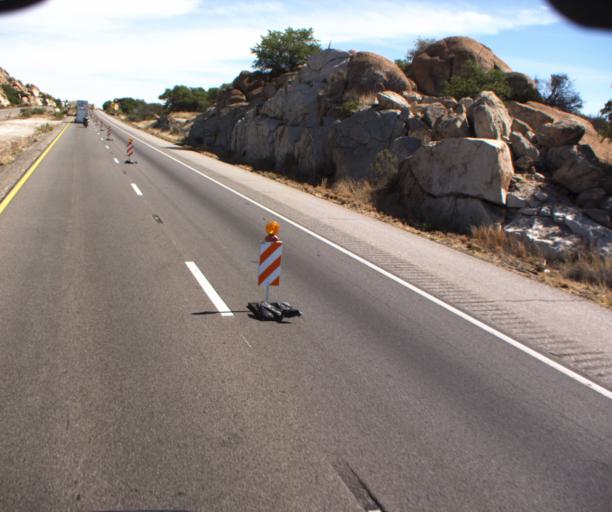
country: US
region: Arizona
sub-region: Cochise County
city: Saint David
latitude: 32.0495
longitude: -110.0867
